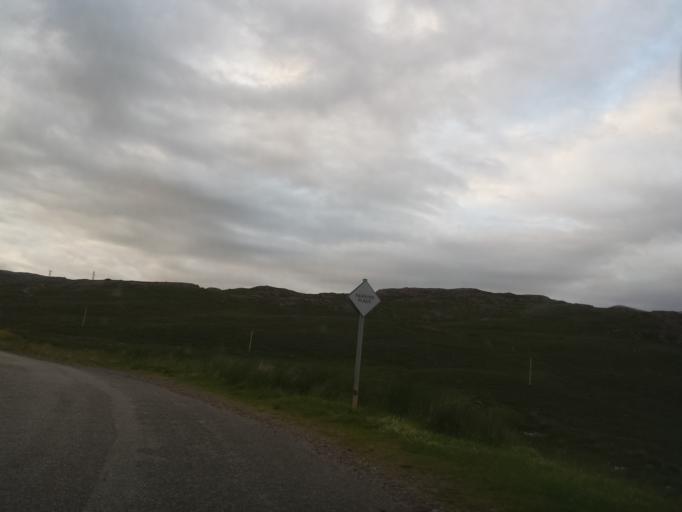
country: GB
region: Scotland
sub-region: Highland
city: Ullapool
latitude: 57.4689
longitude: -5.5858
